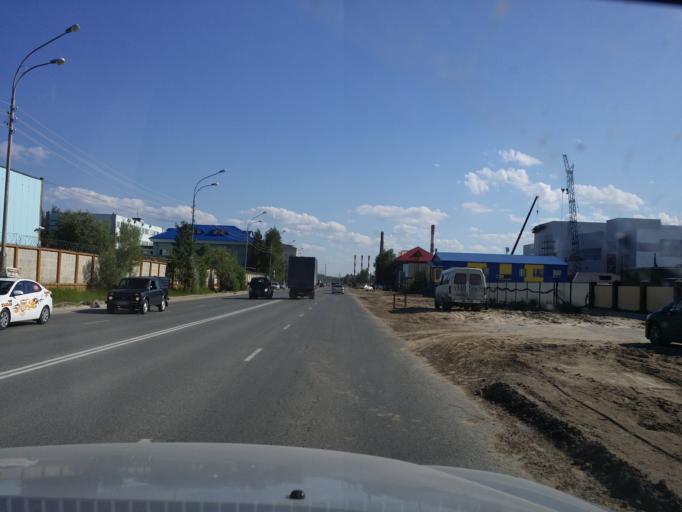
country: RU
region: Khanty-Mansiyskiy Avtonomnyy Okrug
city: Nizhnevartovsk
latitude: 60.9429
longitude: 76.5482
